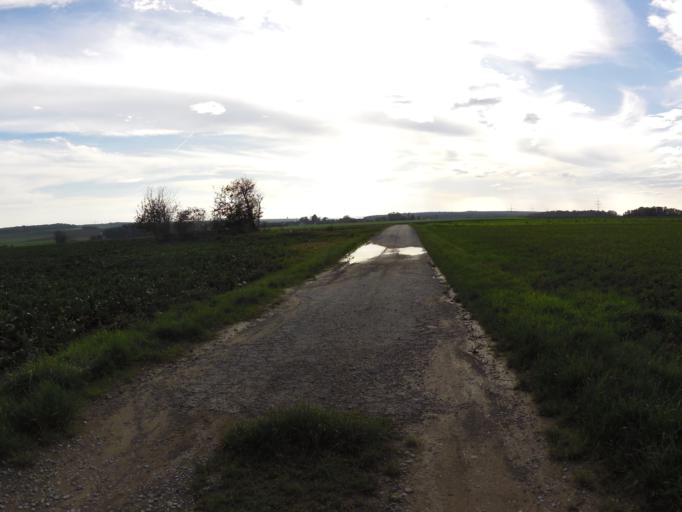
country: DE
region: Bavaria
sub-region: Regierungsbezirk Unterfranken
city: Frickenhausen
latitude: 49.7163
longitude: 10.0777
